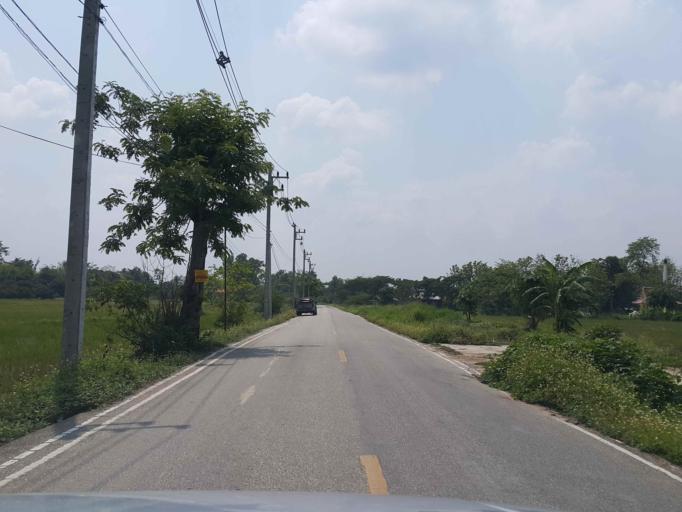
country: TH
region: Chiang Mai
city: Hang Dong
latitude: 18.7022
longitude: 98.9681
